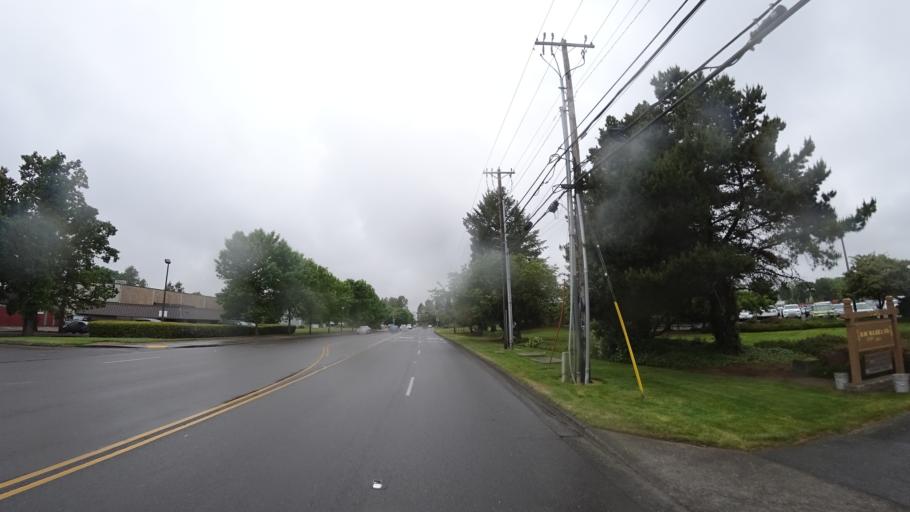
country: US
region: Oregon
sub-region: Washington County
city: Raleigh Hills
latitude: 45.4748
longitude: -122.7793
